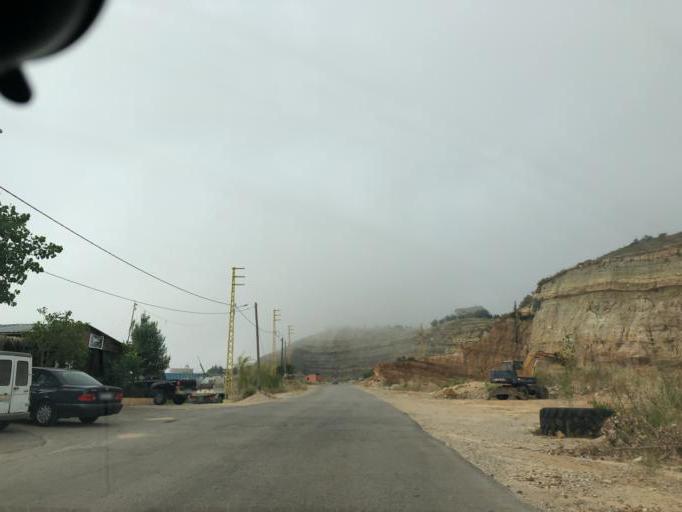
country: LB
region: Mont-Liban
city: Jbail
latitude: 34.0285
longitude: 35.7746
